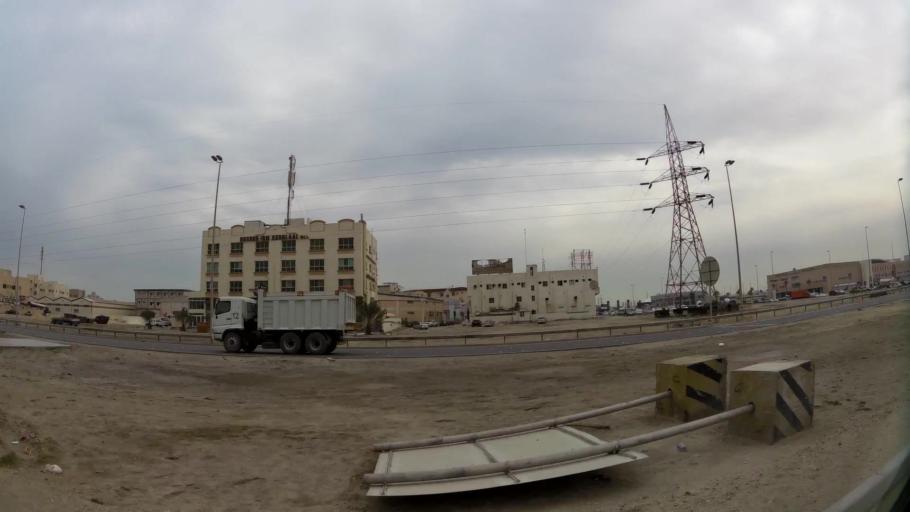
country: BH
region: Northern
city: Sitrah
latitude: 26.1731
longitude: 50.6014
